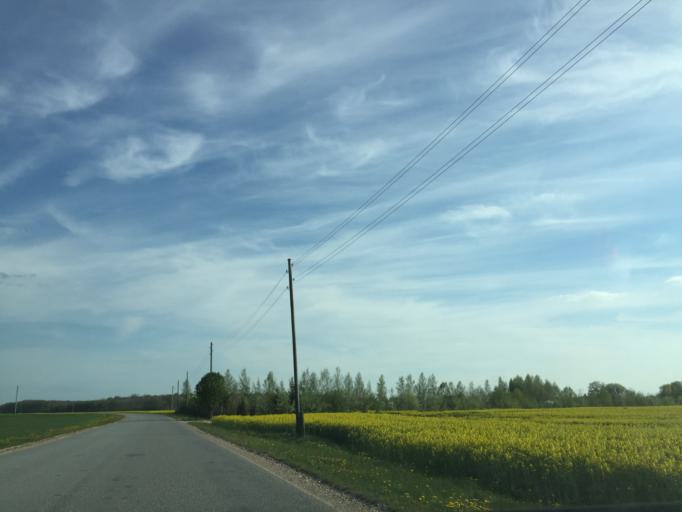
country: LV
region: Bauskas Rajons
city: Bauska
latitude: 56.3897
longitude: 24.2057
